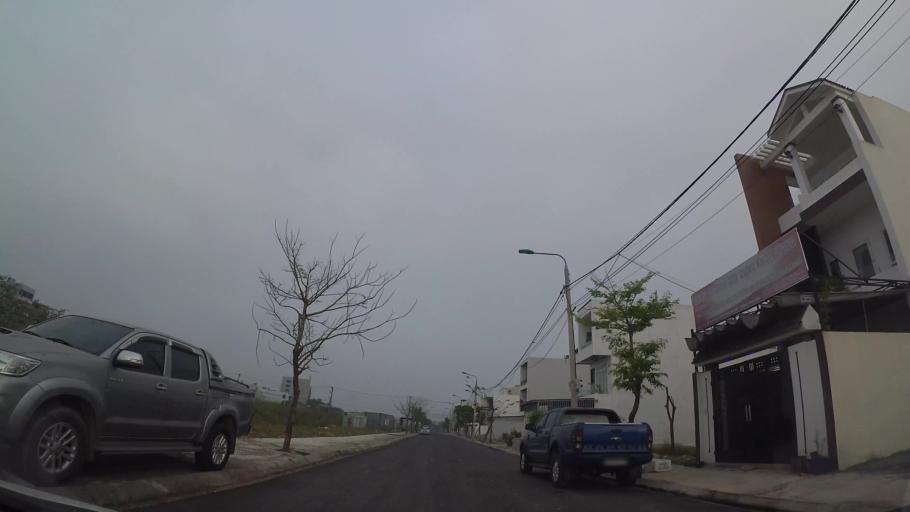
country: VN
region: Da Nang
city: Ngu Hanh Son
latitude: 16.0186
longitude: 108.2346
